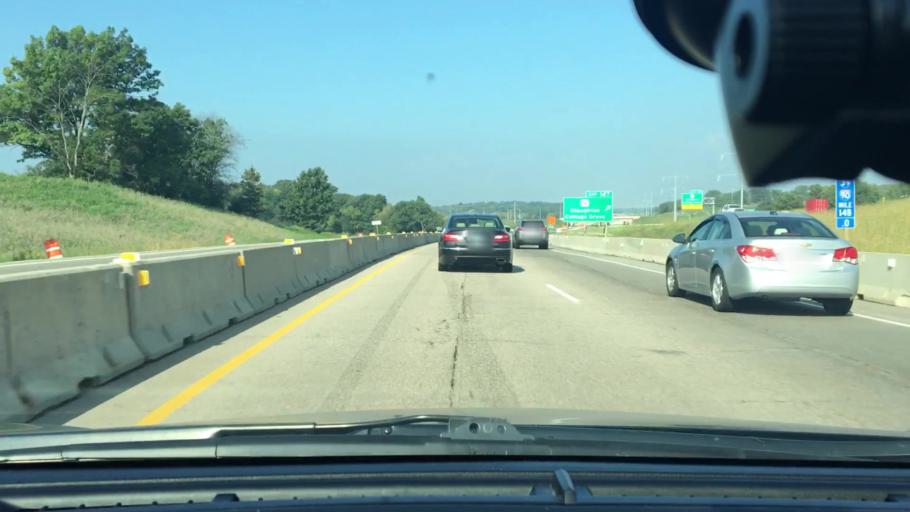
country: US
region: Wisconsin
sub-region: Dane County
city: Cottage Grove
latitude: 42.9984
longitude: -89.1907
